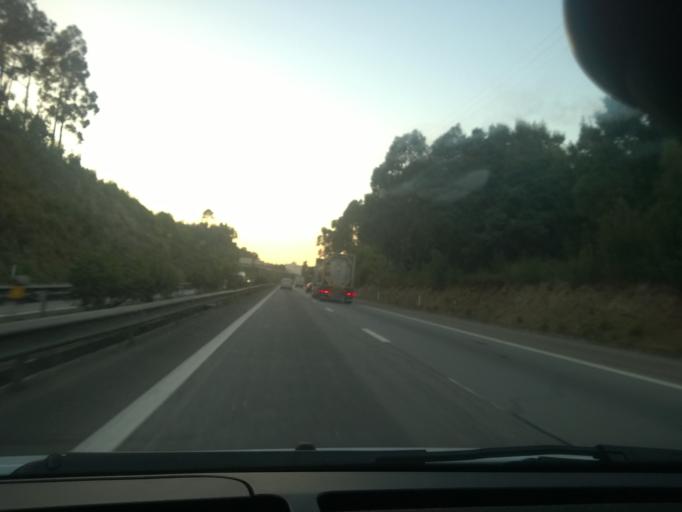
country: PT
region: Porto
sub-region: Vila Nova de Gaia
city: Avintes
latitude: 41.1109
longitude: -8.5670
